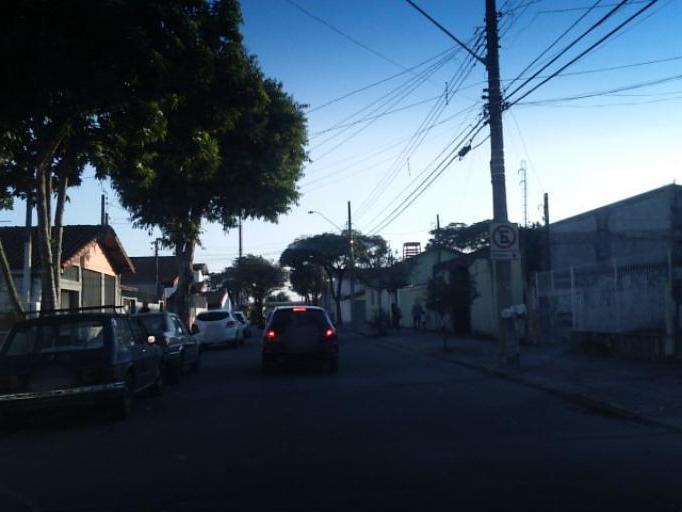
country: BR
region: Sao Paulo
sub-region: Sao Jose Dos Campos
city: Sao Jose dos Campos
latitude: -23.1631
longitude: -45.8931
